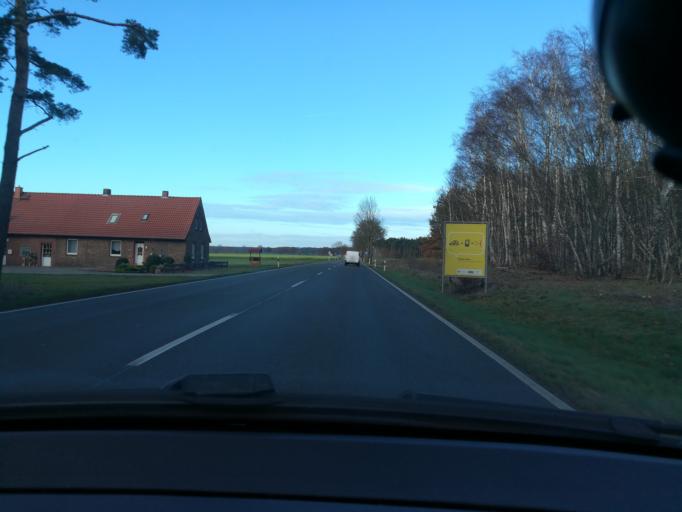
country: DE
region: Lower Saxony
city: Kirchdorf
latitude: 52.5497
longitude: 8.8618
